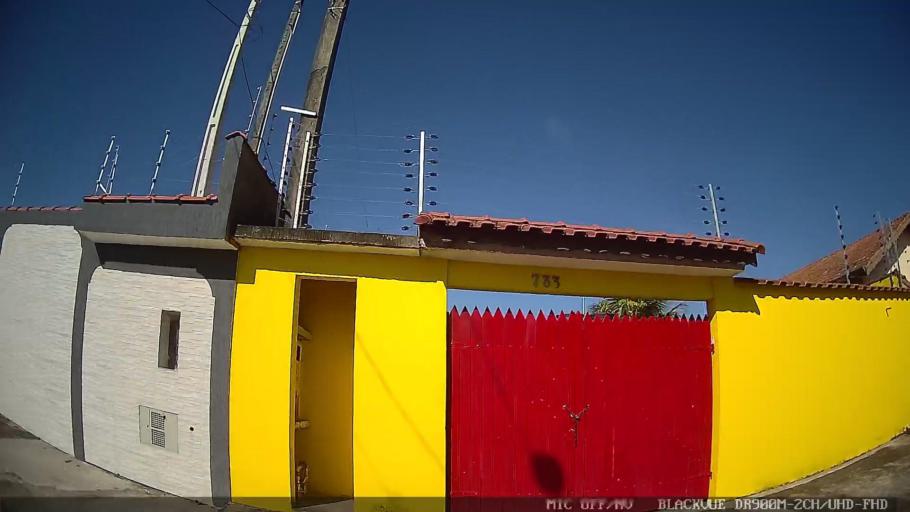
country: BR
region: Sao Paulo
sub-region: Peruibe
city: Peruibe
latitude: -24.2758
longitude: -46.9475
